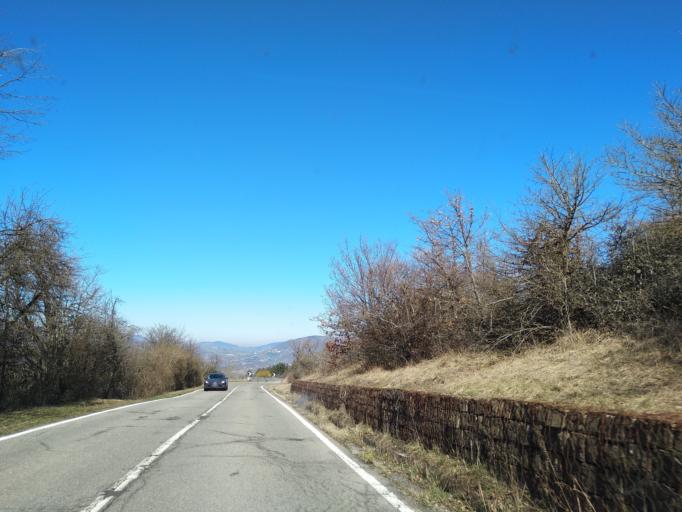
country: IT
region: Emilia-Romagna
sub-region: Provincia di Reggio Emilia
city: Busana
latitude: 44.4068
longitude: 10.3265
